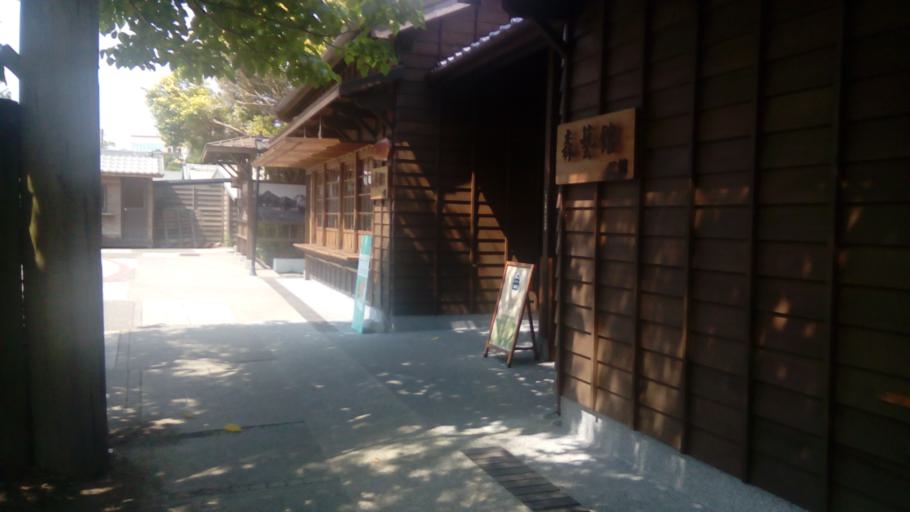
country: TW
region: Taiwan
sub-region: Yilan
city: Yilan
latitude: 24.6855
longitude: 121.7725
